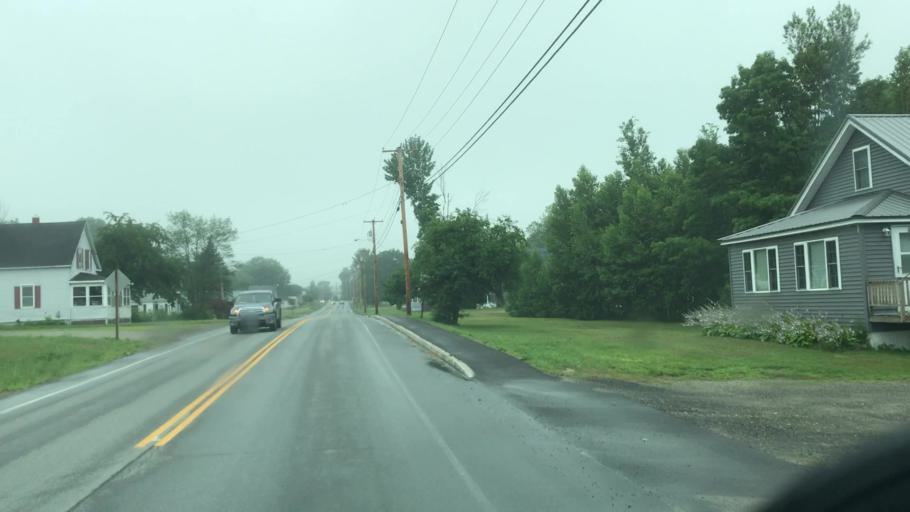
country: US
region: Maine
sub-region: Penobscot County
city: Howland
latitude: 45.2386
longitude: -68.6611
